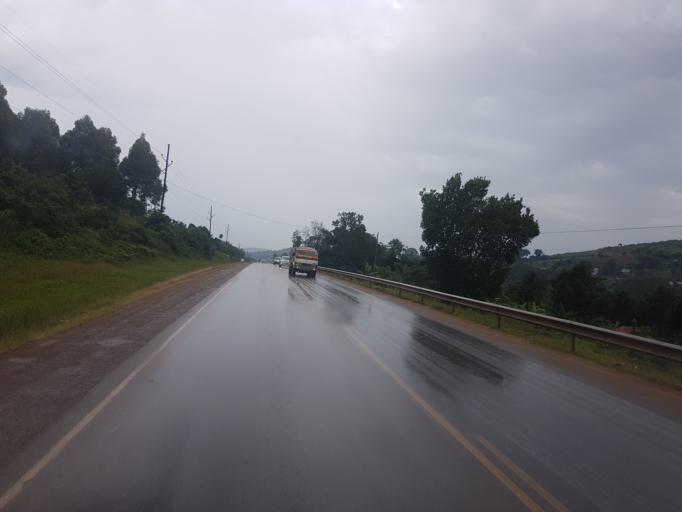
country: UG
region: Central Region
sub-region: Mpigi District
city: Mpigi
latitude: 0.1980
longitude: 32.2988
